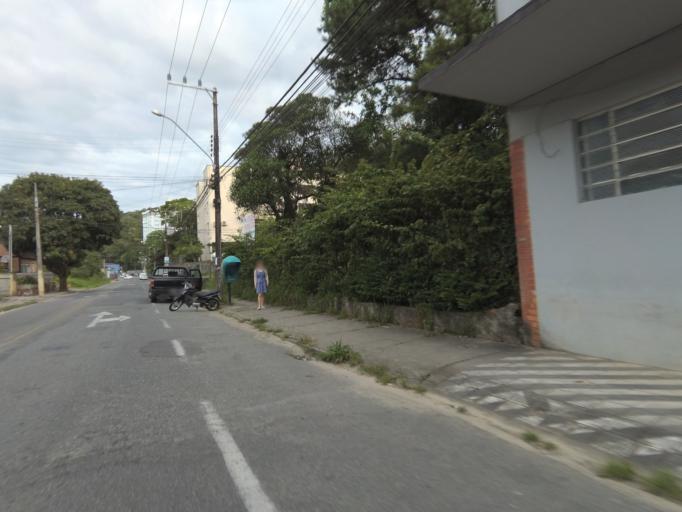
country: BR
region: Santa Catarina
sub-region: Blumenau
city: Blumenau
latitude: -26.9261
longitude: -49.0528
